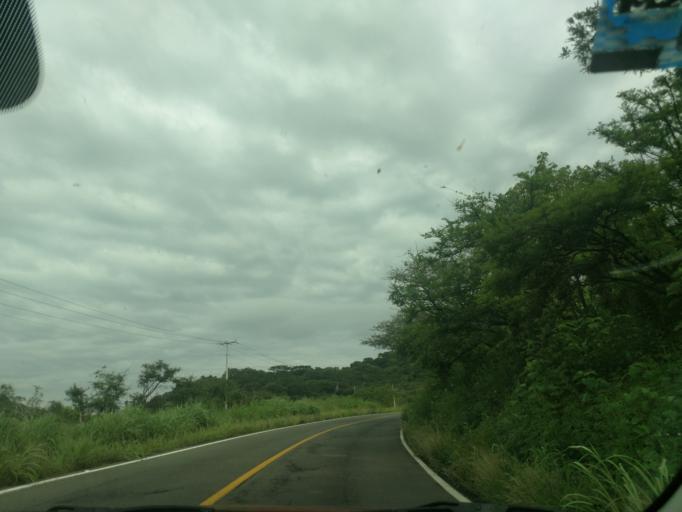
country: MX
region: Jalisco
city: Ameca
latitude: 20.5418
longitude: -104.2780
